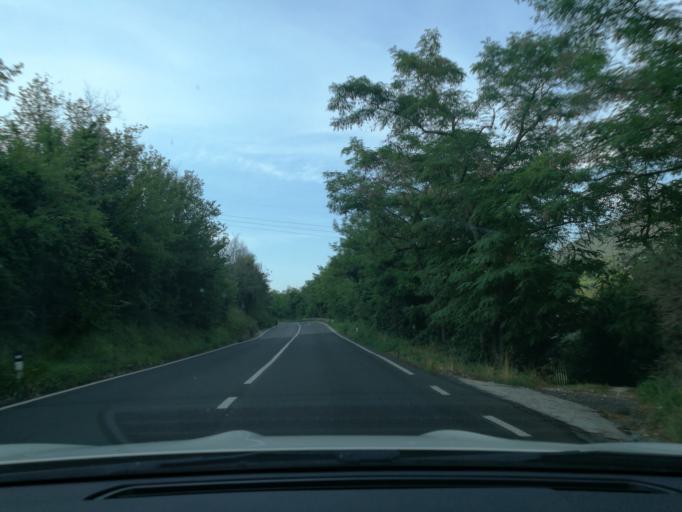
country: IT
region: Umbria
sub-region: Provincia di Terni
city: San Gemini
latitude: 42.6271
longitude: 12.5515
